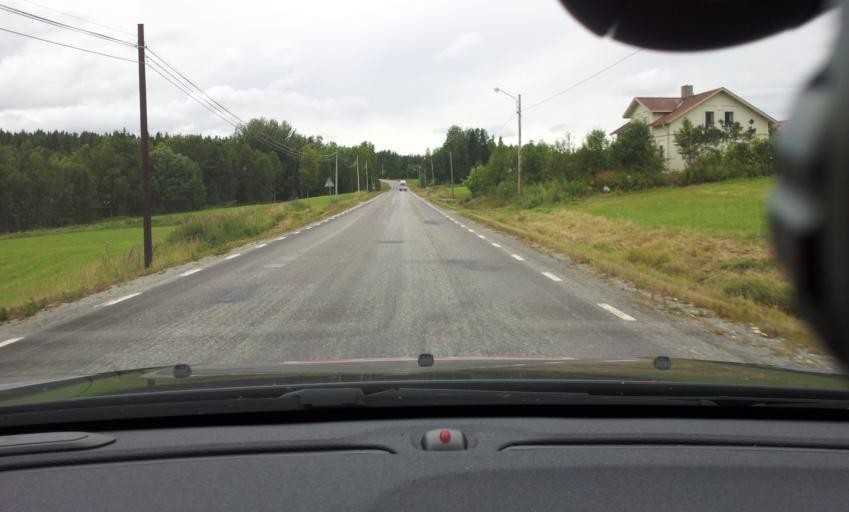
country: SE
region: Jaemtland
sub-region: Braecke Kommun
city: Braecke
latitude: 62.9737
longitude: 15.1857
